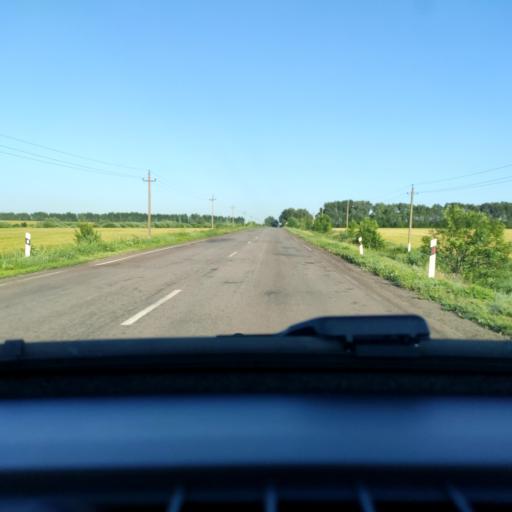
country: RU
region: Voronezj
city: Kashirskoye
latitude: 51.4930
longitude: 39.8436
